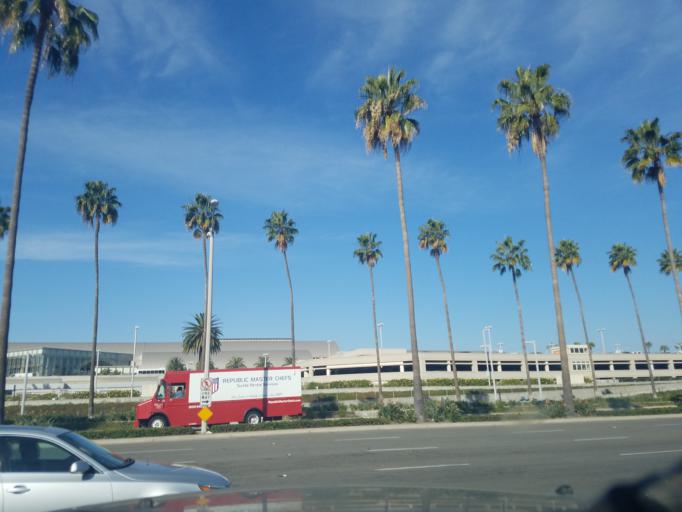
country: US
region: California
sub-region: Orange County
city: Irvine
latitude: 33.6788
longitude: -117.8595
